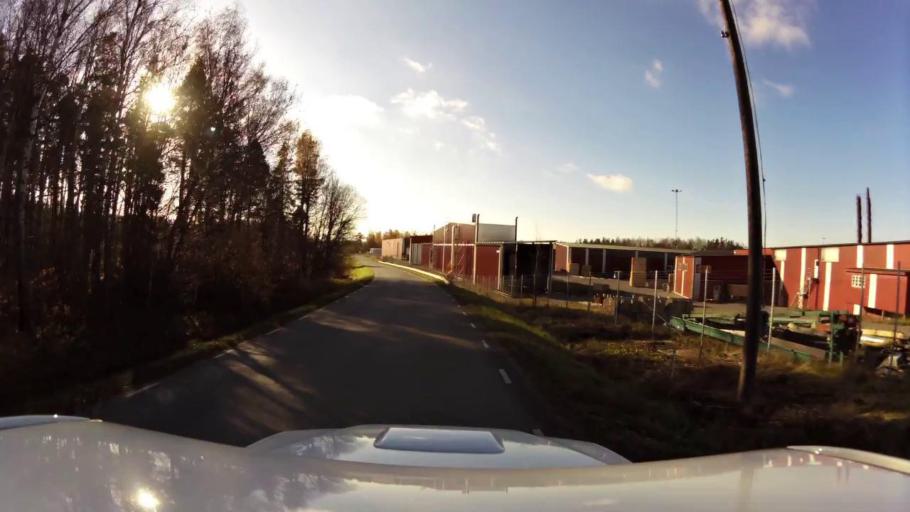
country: SE
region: OEstergoetland
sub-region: Linkopings Kommun
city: Linghem
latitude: 58.4415
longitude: 15.7791
